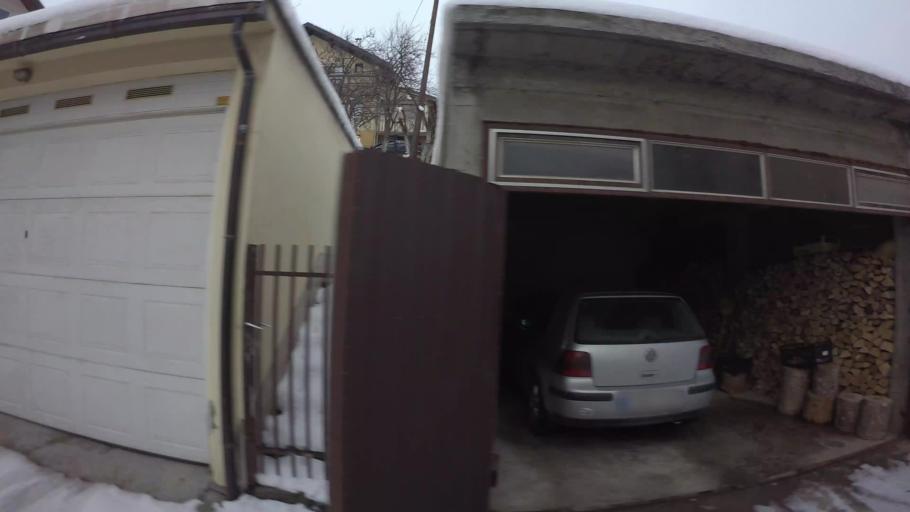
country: BA
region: Federation of Bosnia and Herzegovina
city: Kobilja Glava
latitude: 43.8636
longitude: 18.3919
